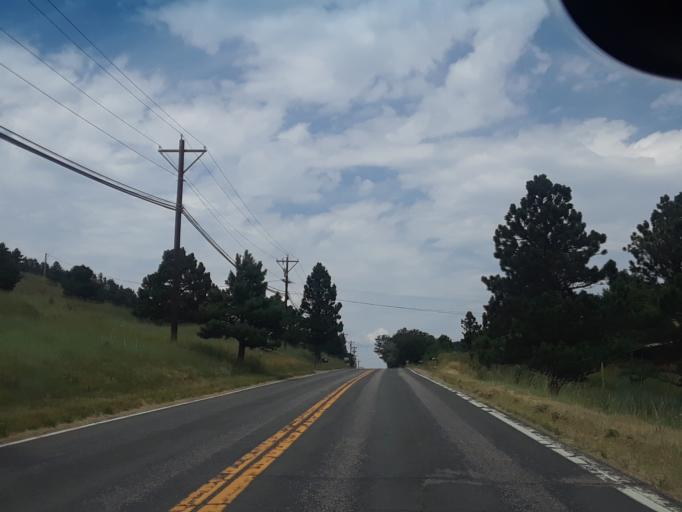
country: US
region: Colorado
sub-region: Boulder County
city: Boulder
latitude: 40.0752
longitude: -105.3013
